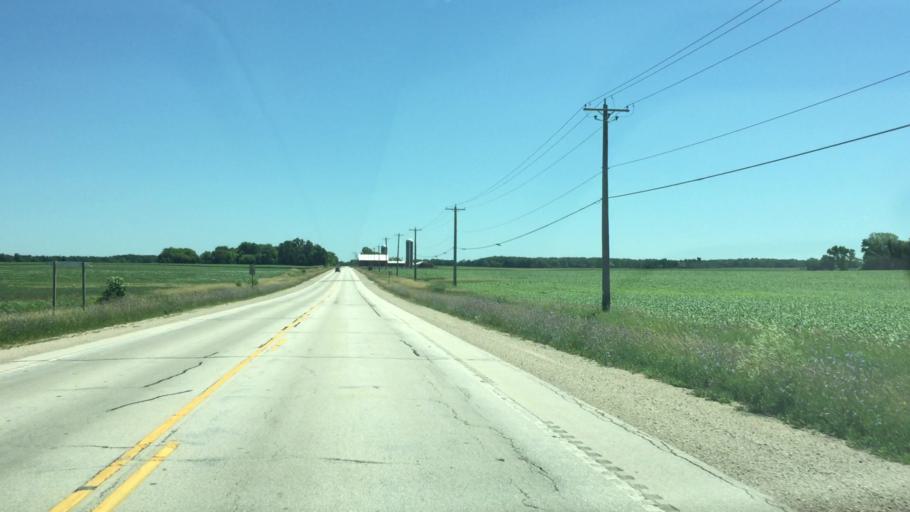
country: US
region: Wisconsin
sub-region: Calumet County
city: Hilbert
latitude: 44.1403
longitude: -88.2017
